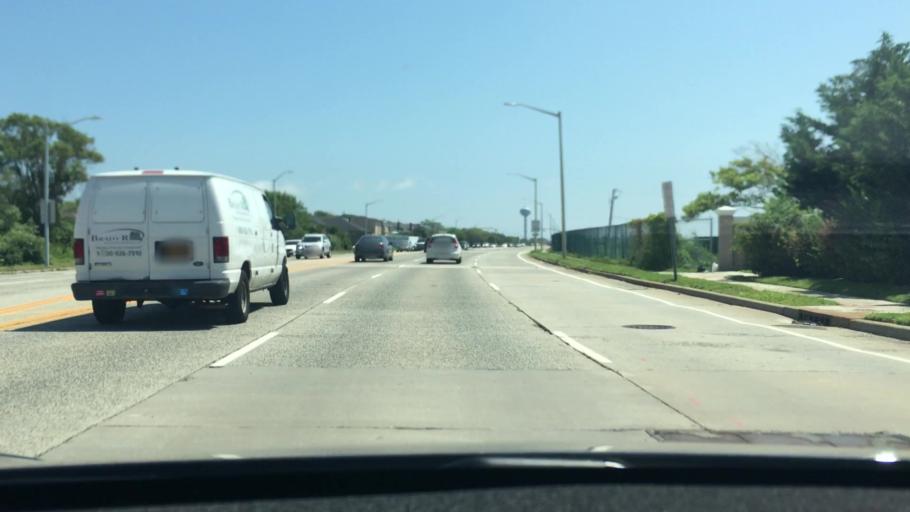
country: US
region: New York
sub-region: Nassau County
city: Lido Beach
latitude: 40.5918
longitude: -73.6102
